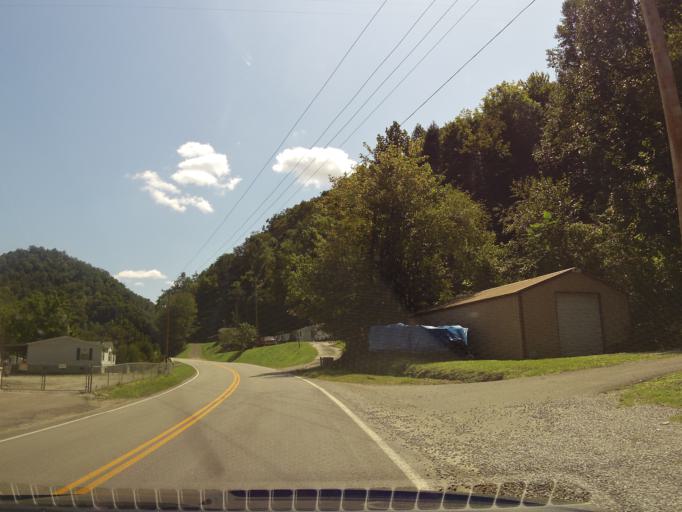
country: US
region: Kentucky
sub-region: Leslie County
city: Hyden
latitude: 37.0806
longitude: -83.3969
